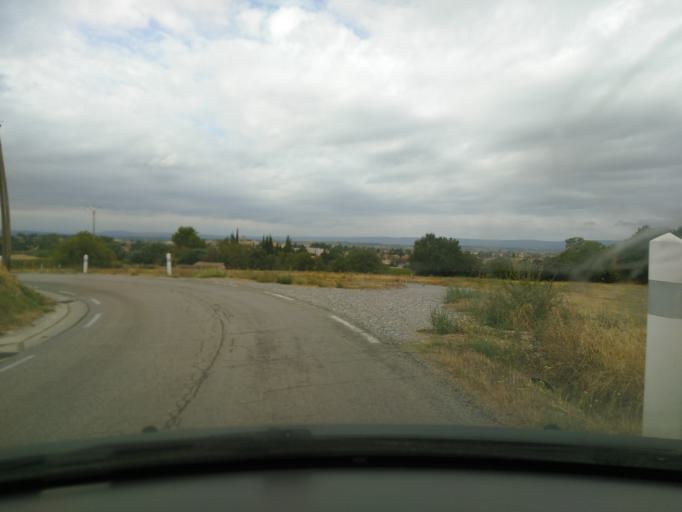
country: FR
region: Provence-Alpes-Cote d'Azur
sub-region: Departement du Vaucluse
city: Valreas
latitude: 44.3763
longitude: 5.0047
